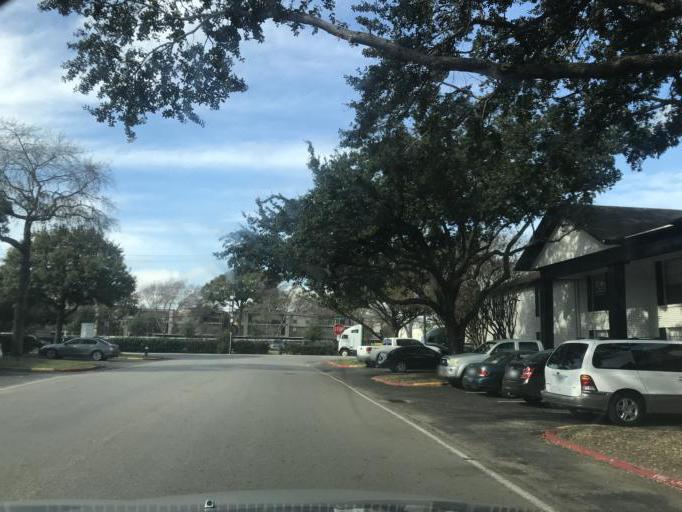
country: US
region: Texas
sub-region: Harris County
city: Hunters Creek Village
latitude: 29.7354
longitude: -95.4892
